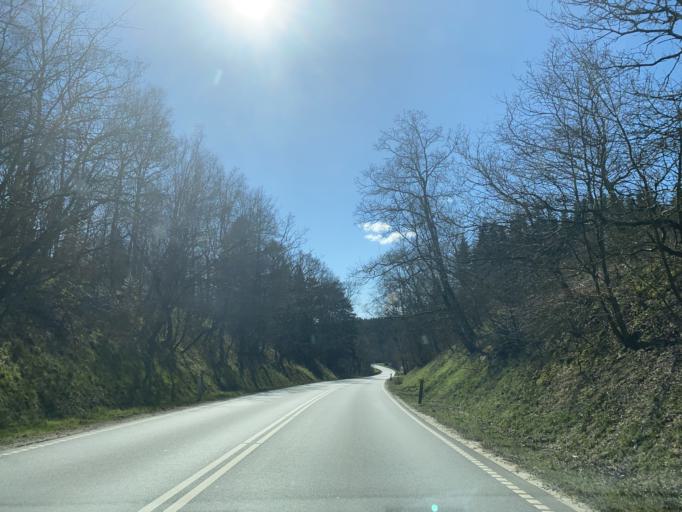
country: DK
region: Central Jutland
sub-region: Viborg Kommune
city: Bjerringbro
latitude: 56.2680
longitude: 9.6201
